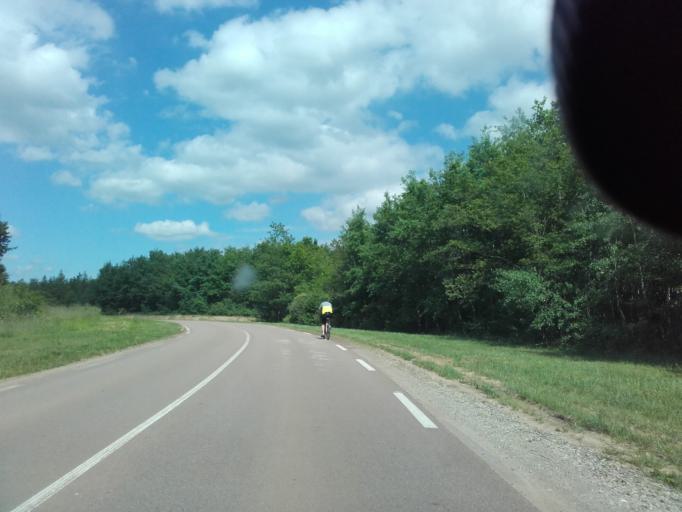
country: FR
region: Bourgogne
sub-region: Departement de Saone-et-Loire
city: Fontaines
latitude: 46.8854
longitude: 4.7819
